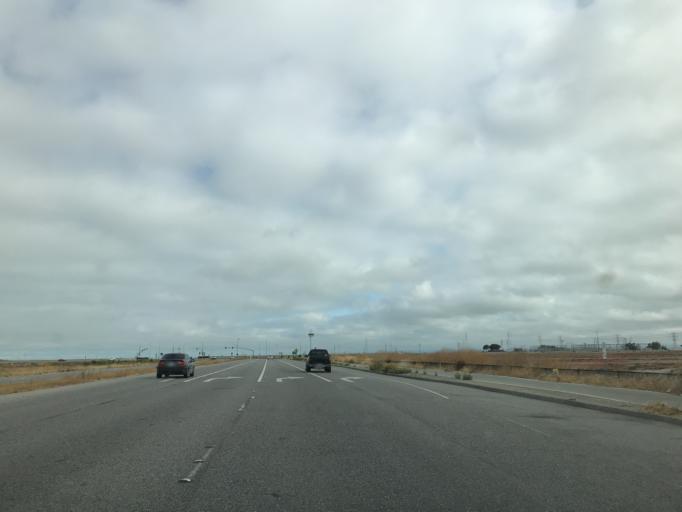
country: US
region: California
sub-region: San Mateo County
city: East Palo Alto
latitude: 37.4829
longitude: -122.1403
